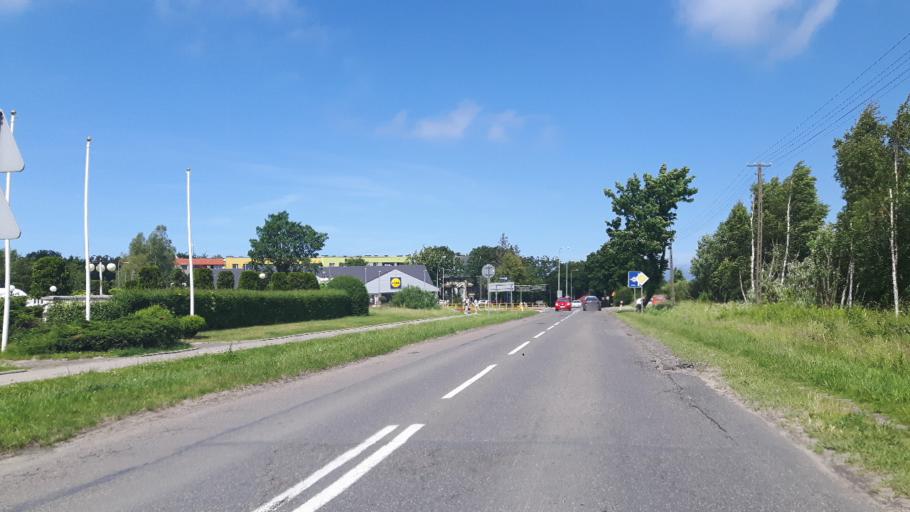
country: PL
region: Pomeranian Voivodeship
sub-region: Powiat slupski
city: Ustka
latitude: 54.5743
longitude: 16.8524
